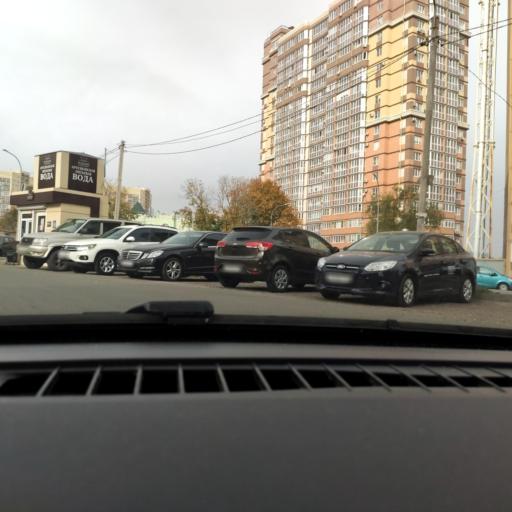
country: RU
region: Voronezj
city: Voronezh
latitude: 51.7024
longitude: 39.2069
